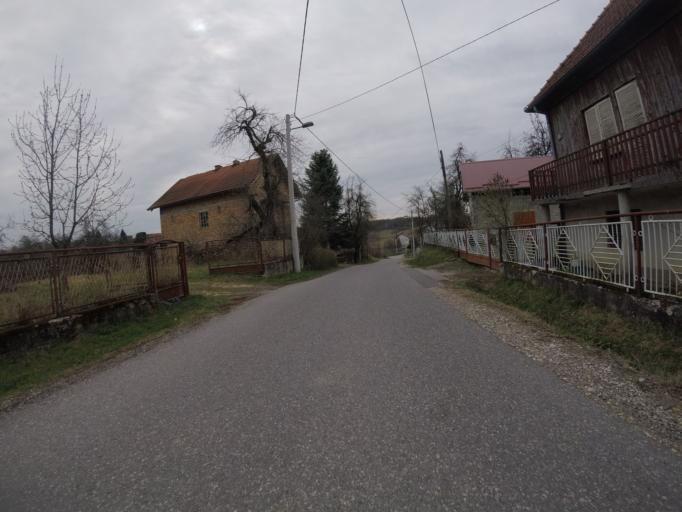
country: HR
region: Grad Zagreb
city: Strmec
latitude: 45.6257
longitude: 15.9345
